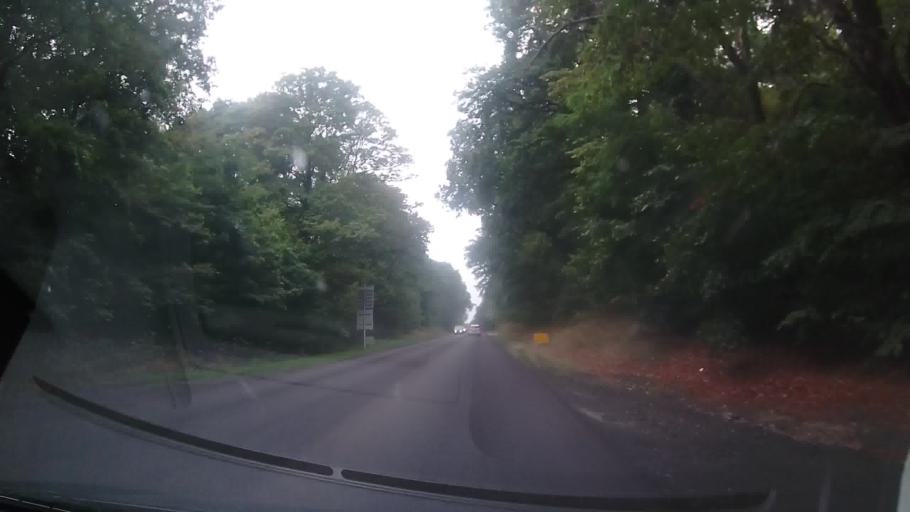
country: FR
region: Ile-de-France
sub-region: Departement de l'Essonne
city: Dourdan
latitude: 48.5403
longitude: 1.9988
